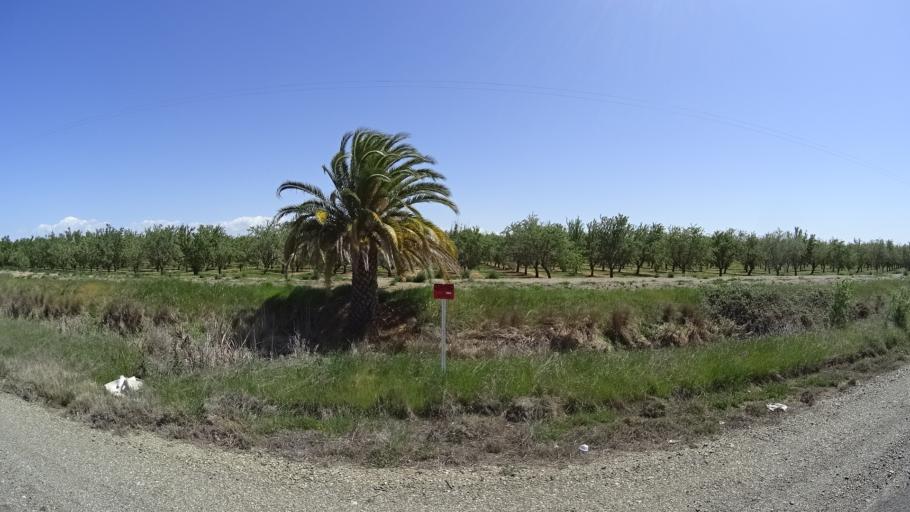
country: US
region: California
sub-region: Glenn County
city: Orland
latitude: 39.7947
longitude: -122.1410
